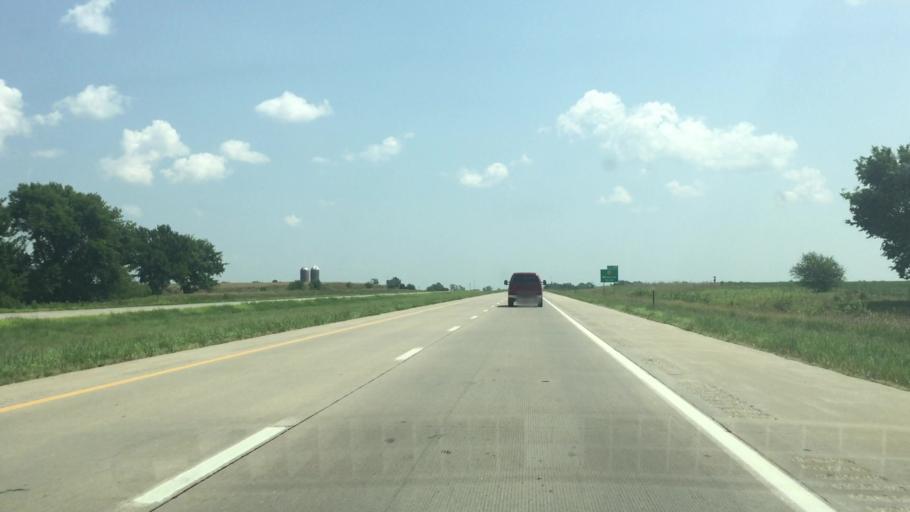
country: US
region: Kansas
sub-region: Franklin County
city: Wellsville
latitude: 38.6990
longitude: -95.0942
